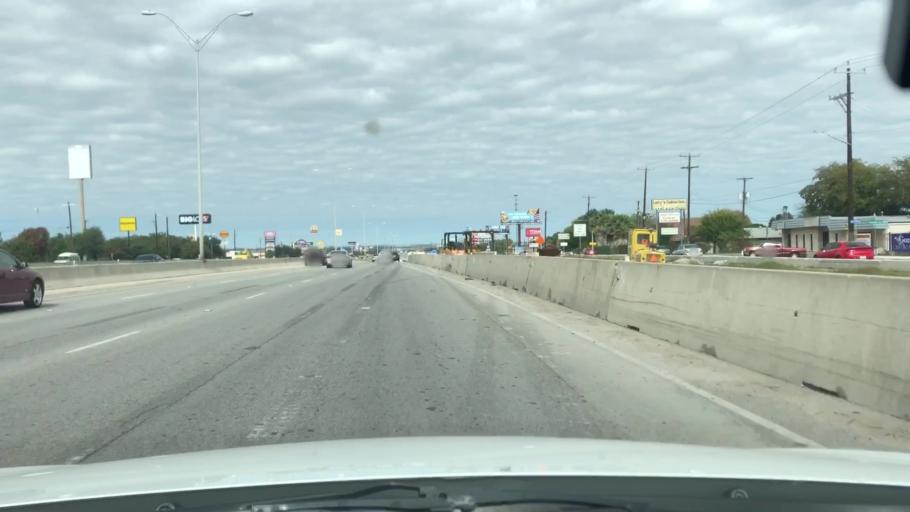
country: US
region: Texas
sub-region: Bexar County
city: Lackland Air Force Base
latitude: 29.4110
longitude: -98.6495
